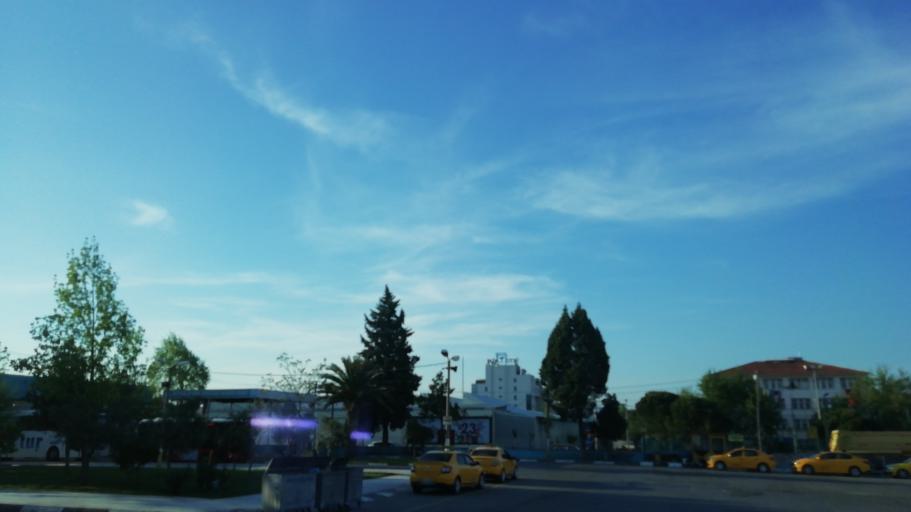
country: TR
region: Manisa
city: Akhisar
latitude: 38.9340
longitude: 27.8358
